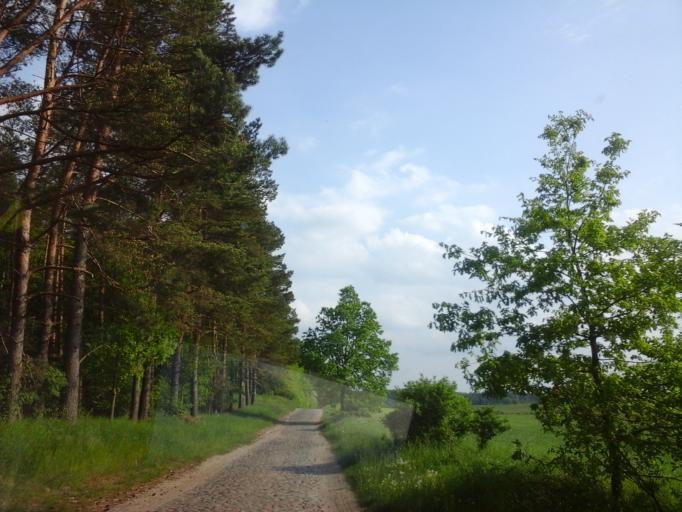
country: PL
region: West Pomeranian Voivodeship
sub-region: Powiat mysliborski
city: Barlinek
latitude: 53.0424
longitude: 15.2150
